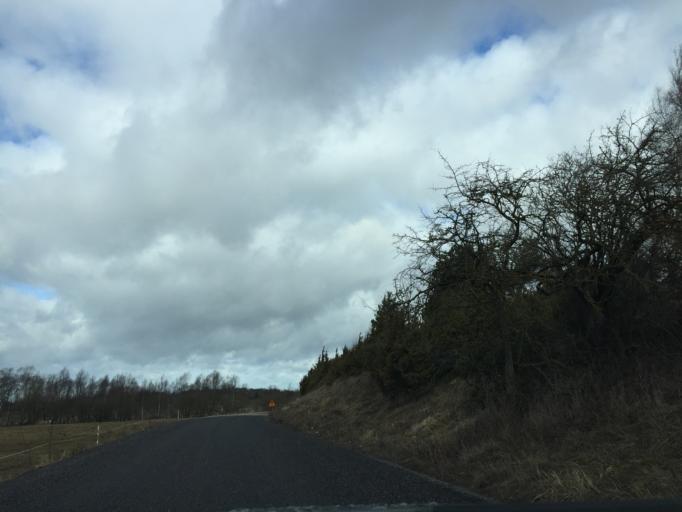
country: EE
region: Laeaene
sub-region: Haapsalu linn
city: Haapsalu
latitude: 58.6772
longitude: 23.5430
